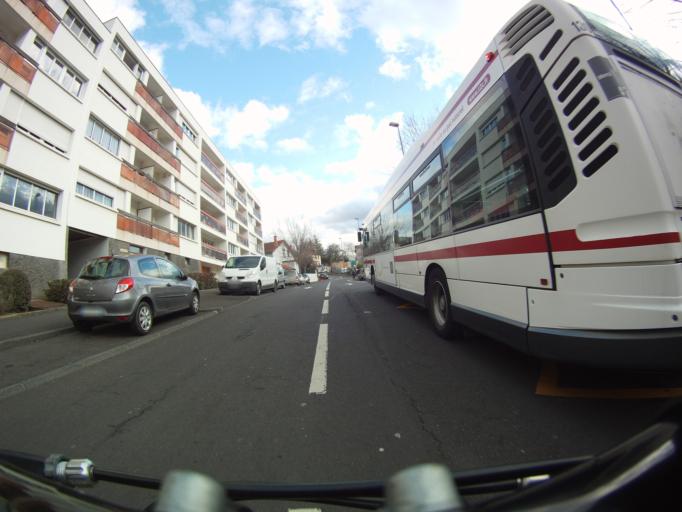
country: FR
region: Auvergne
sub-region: Departement du Puy-de-Dome
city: Beaumont
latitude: 45.7607
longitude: 3.0861
